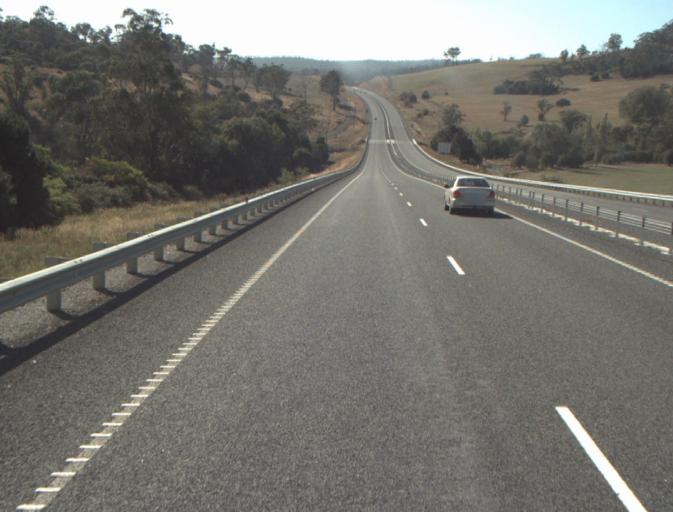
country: AU
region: Tasmania
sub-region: Launceston
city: Mayfield
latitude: -41.3657
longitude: 147.1082
